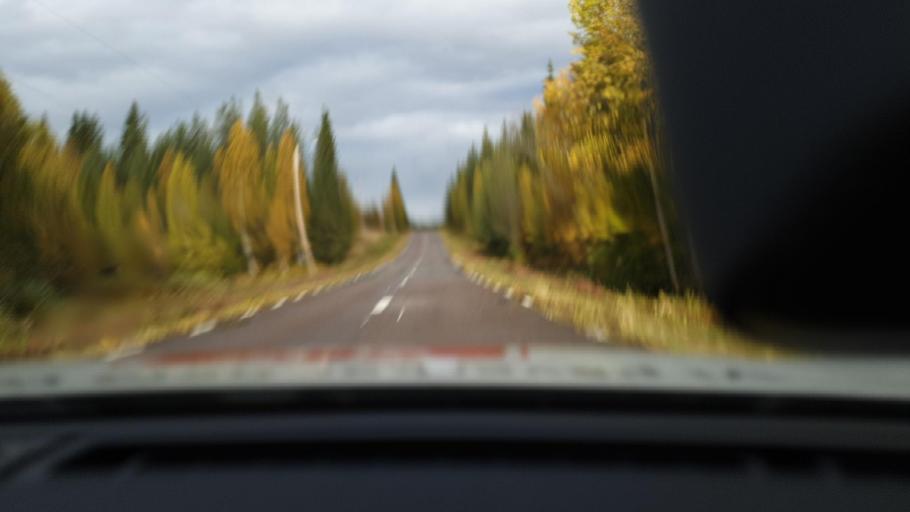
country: SE
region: Norrbotten
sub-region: Overkalix Kommun
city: OEverkalix
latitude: 67.0061
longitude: 22.5183
